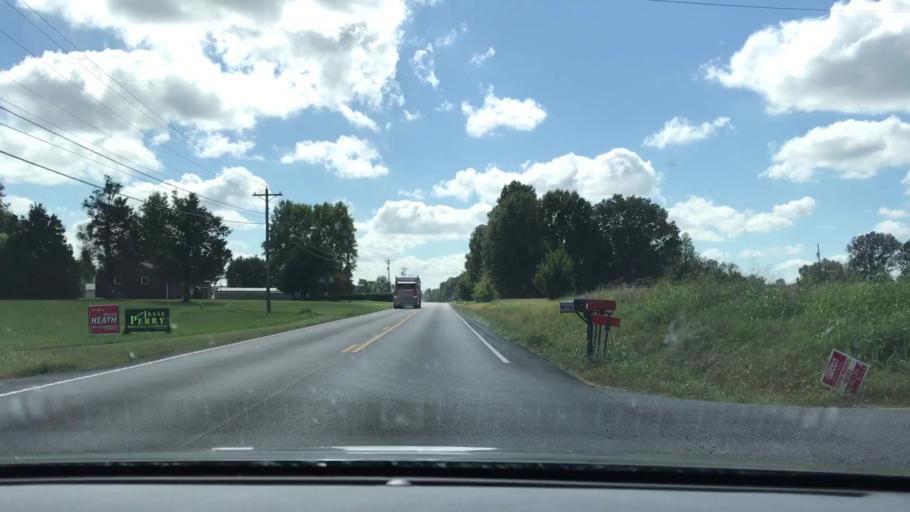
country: US
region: Kentucky
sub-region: Graves County
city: Mayfield
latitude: 36.7660
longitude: -88.5961
